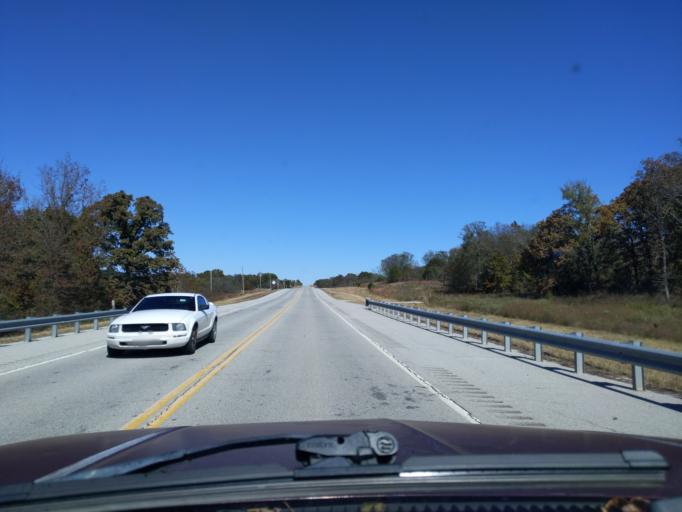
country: US
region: Oklahoma
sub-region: Creek County
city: Bristow
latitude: 35.7367
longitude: -96.3872
